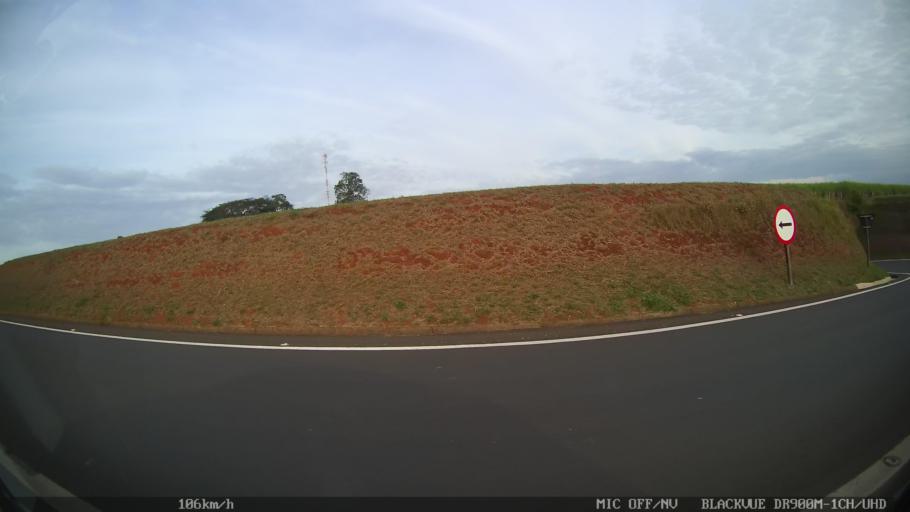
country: BR
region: Sao Paulo
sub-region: Iracemapolis
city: Iracemapolis
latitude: -22.6198
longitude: -47.4876
